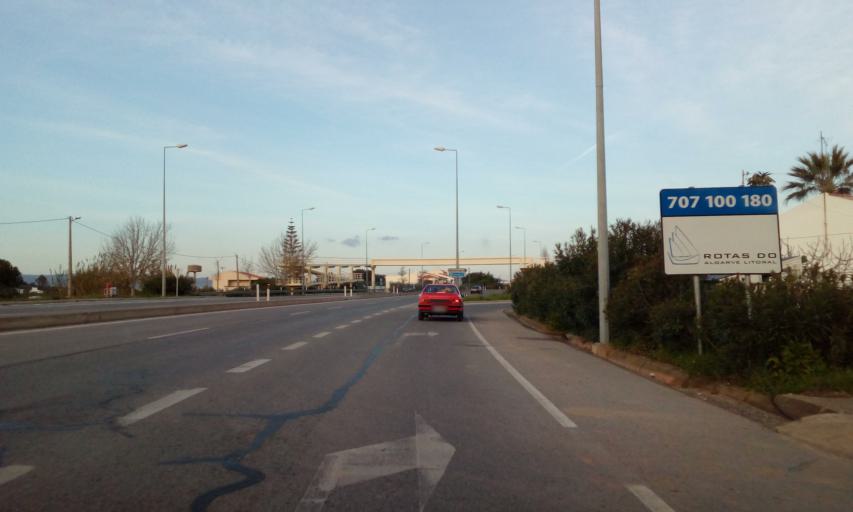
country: PT
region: Faro
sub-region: Faro
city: Faro
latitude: 37.0294
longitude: -7.9687
